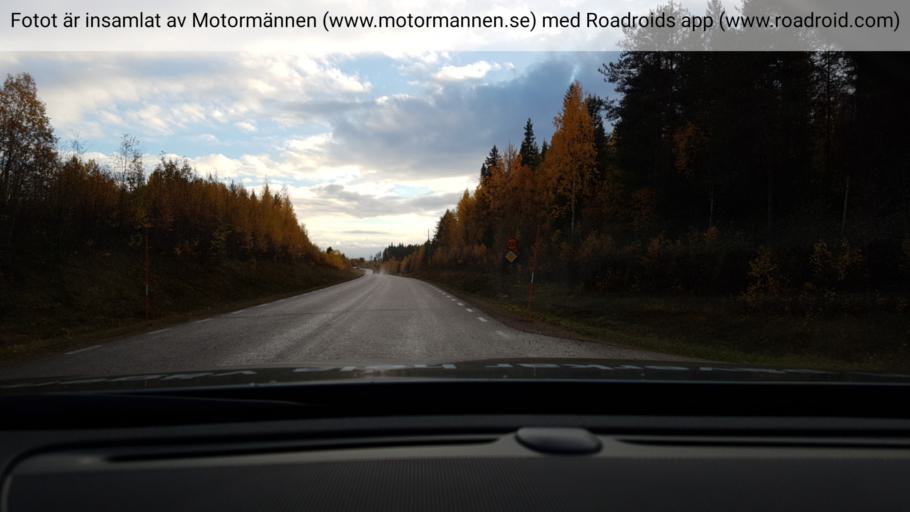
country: SE
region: Norrbotten
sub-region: Overkalix Kommun
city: OEverkalix
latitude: 66.7784
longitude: 22.6981
